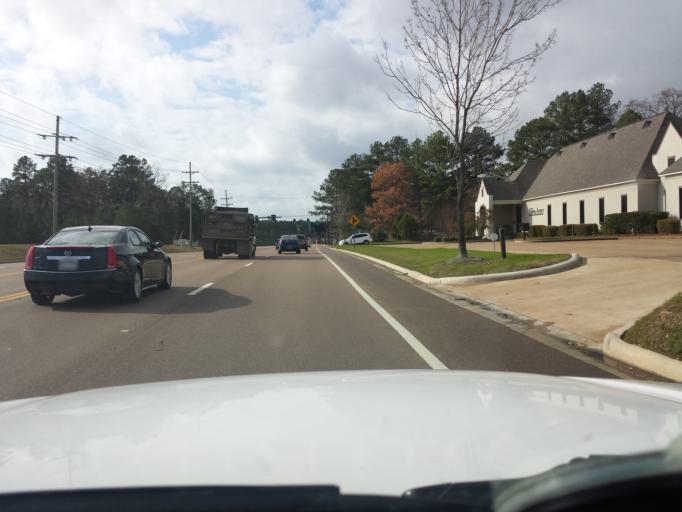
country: US
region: Mississippi
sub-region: Rankin County
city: Flowood
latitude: 32.3581
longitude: -90.0596
